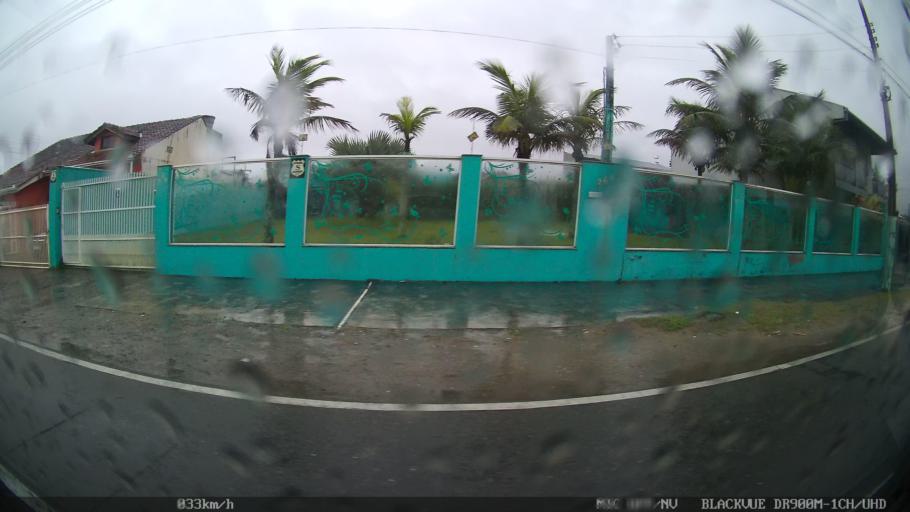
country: BR
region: Santa Catarina
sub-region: Navegantes
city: Navegantes
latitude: -26.8848
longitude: -48.6418
